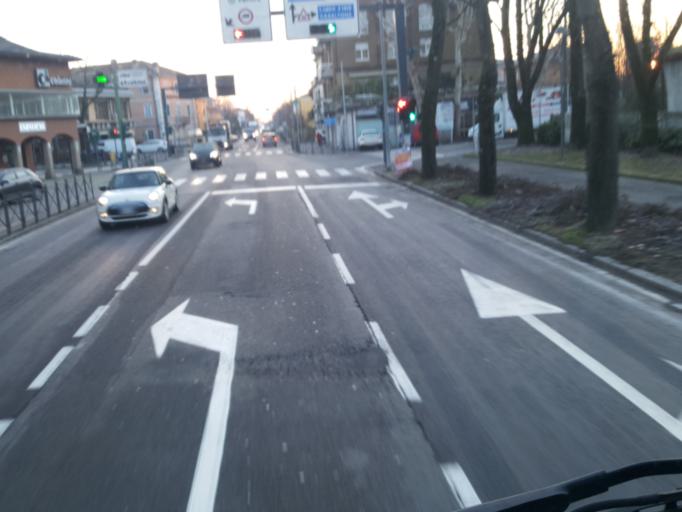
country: IT
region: Emilia-Romagna
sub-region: Provincia di Parma
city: Sorbolo
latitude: 44.8433
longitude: 10.4465
